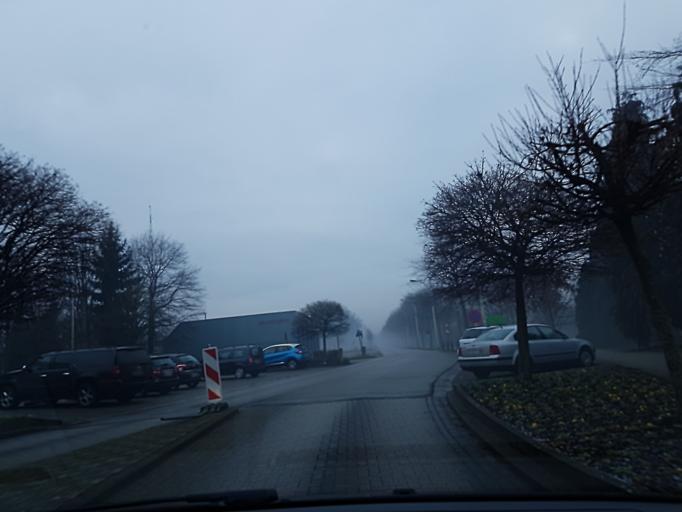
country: BE
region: Flanders
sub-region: Provincie Antwerpen
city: Grobbendonk
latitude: 51.1894
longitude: 4.7383
